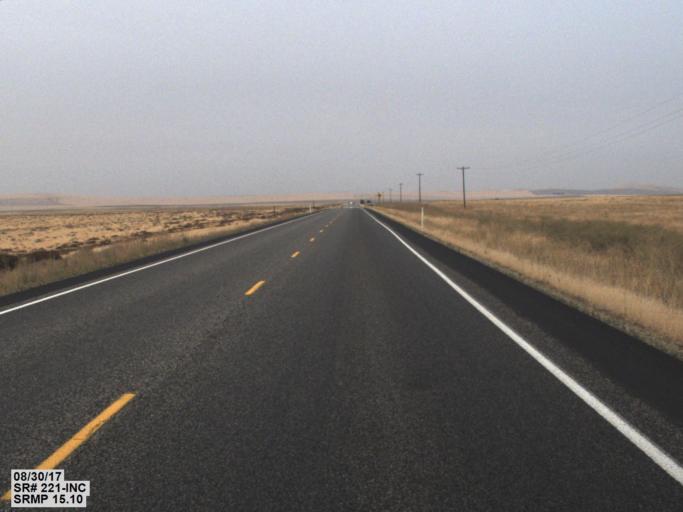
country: US
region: Washington
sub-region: Benton County
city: Benton City
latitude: 46.1538
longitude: -119.6010
